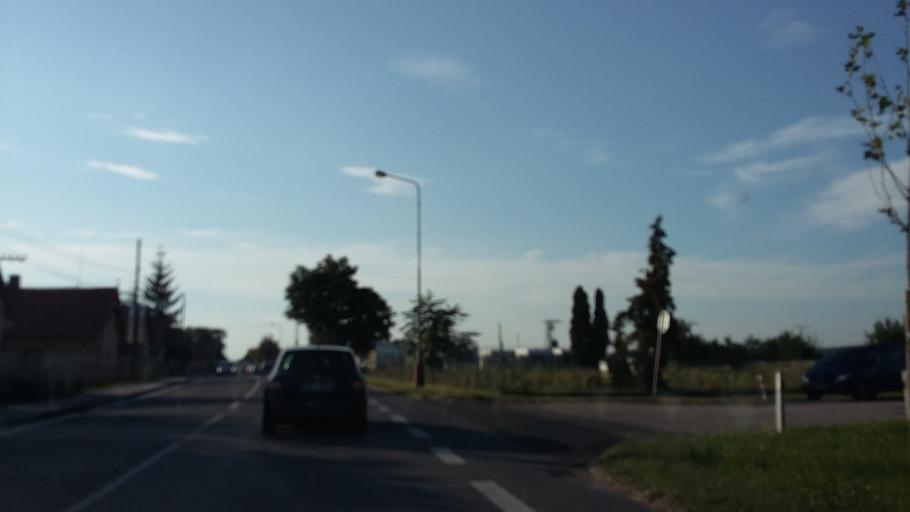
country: CZ
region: Central Bohemia
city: Loucen
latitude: 50.2407
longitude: 15.0198
